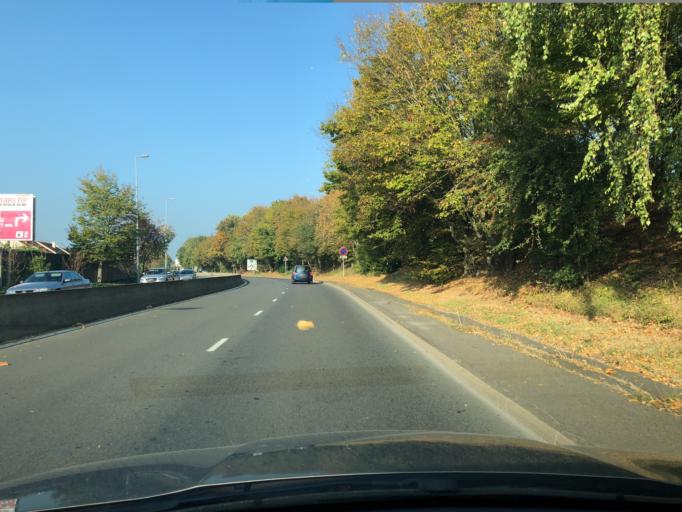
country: FR
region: Centre
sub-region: Departement d'Indre-et-Loire
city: Chanceaux-sur-Choisille
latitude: 47.4316
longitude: 0.7014
